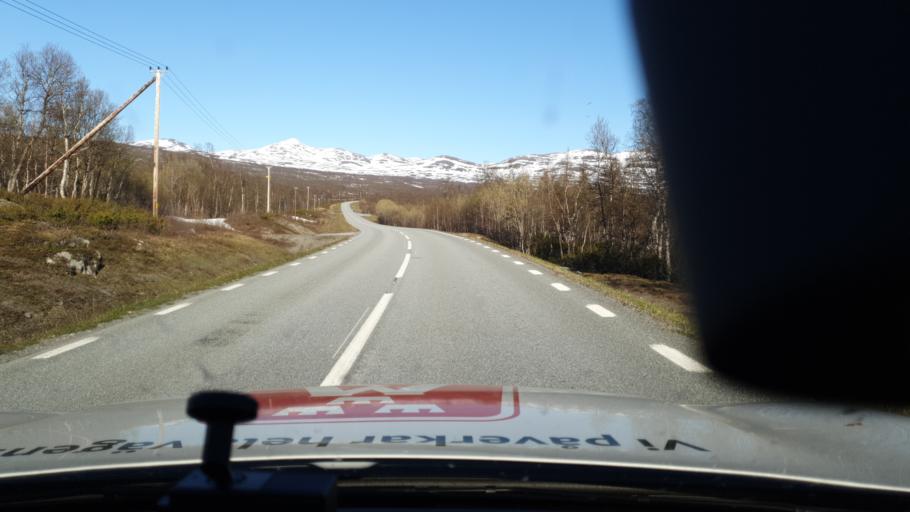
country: NO
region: Nordland
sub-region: Rana
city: Mo i Rana
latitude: 66.0373
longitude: 15.0433
